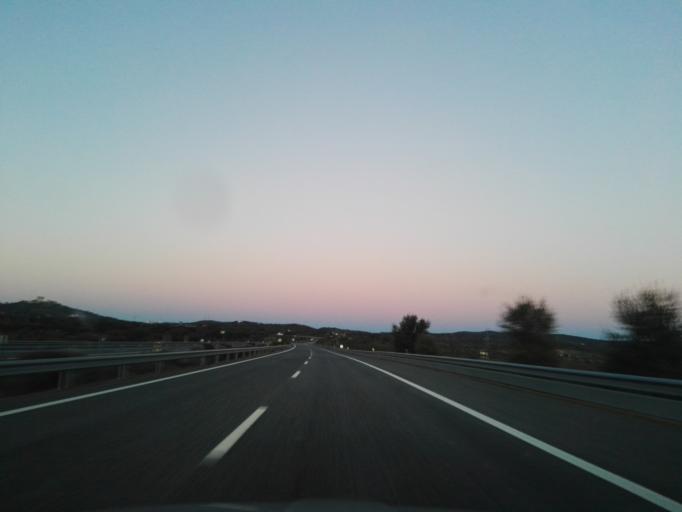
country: PT
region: Evora
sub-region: Estremoz
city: Estremoz
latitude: 38.7461
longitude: -7.7354
